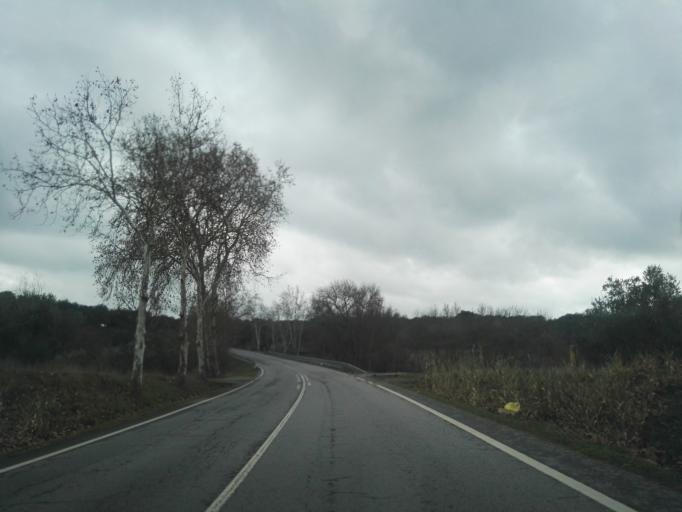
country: PT
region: Portalegre
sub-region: Arronches
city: Arronches
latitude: 39.1284
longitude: -7.2952
